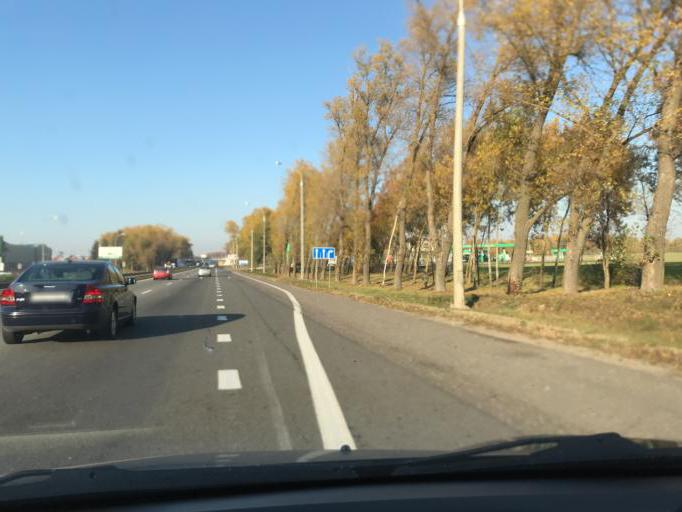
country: BY
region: Minsk
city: Yubilyeyny
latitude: 53.8097
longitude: 27.5296
